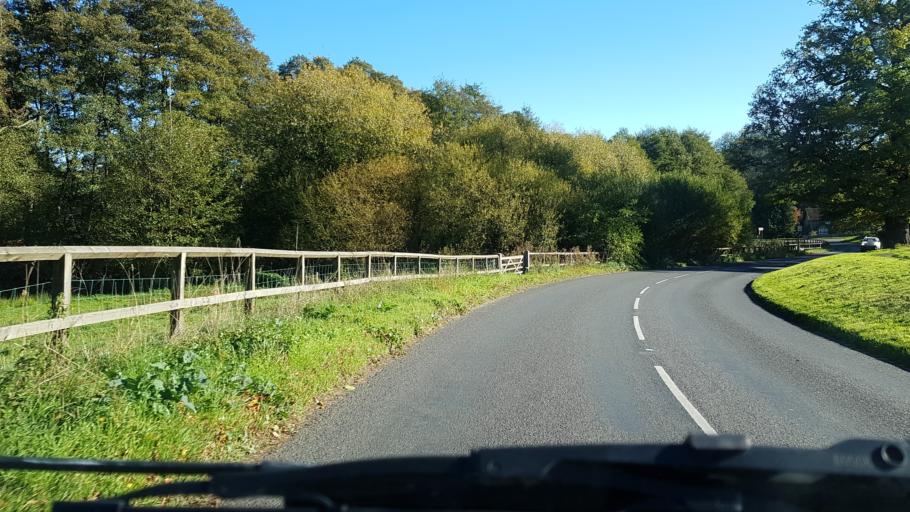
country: GB
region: England
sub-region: Surrey
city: Chilworth
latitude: 51.2210
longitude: -0.4893
